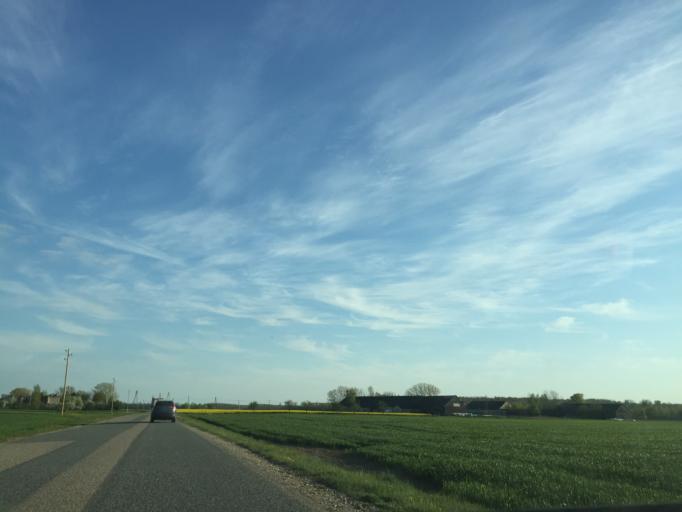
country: LV
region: Bauskas Rajons
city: Bauska
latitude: 56.3008
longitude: 24.2612
